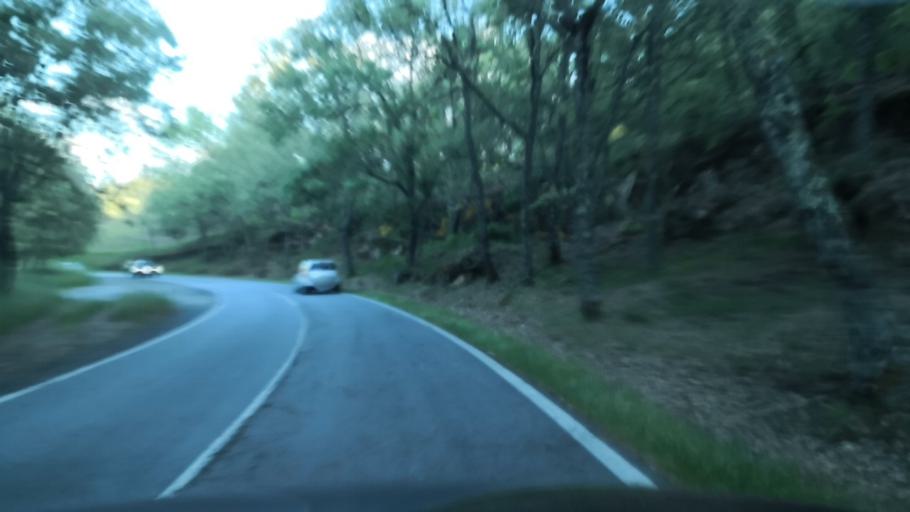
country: PT
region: Portalegre
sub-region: Marvao
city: Marvao
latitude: 39.3660
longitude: -7.3980
